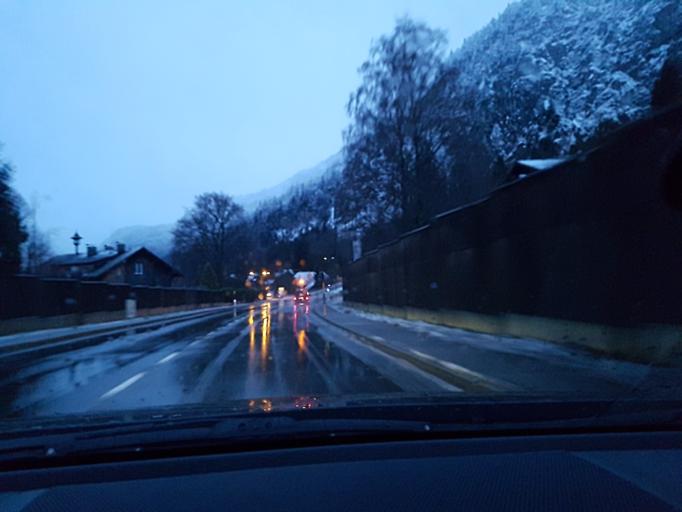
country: AT
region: Salzburg
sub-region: Politischer Bezirk Salzburg-Umgebung
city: Sankt Gilgen
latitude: 47.7619
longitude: 13.3669
